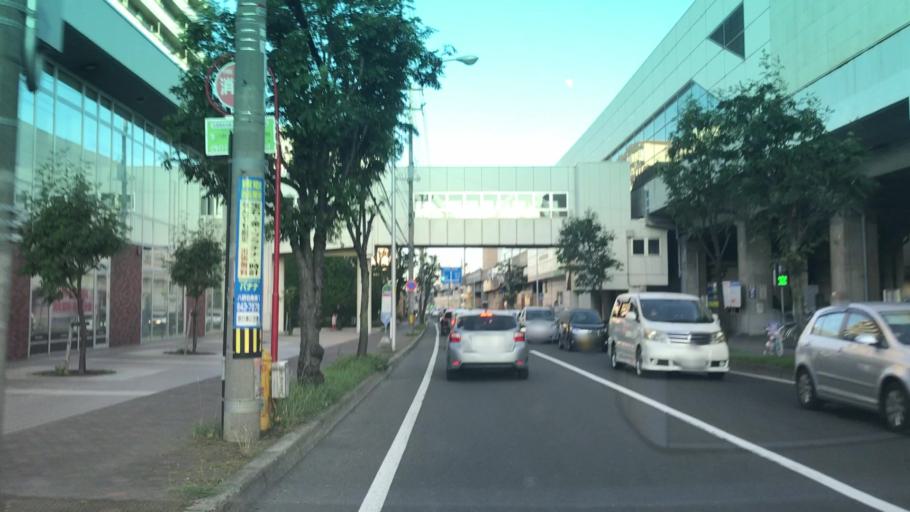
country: JP
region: Hokkaido
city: Sapporo
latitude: 43.0822
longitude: 141.3066
